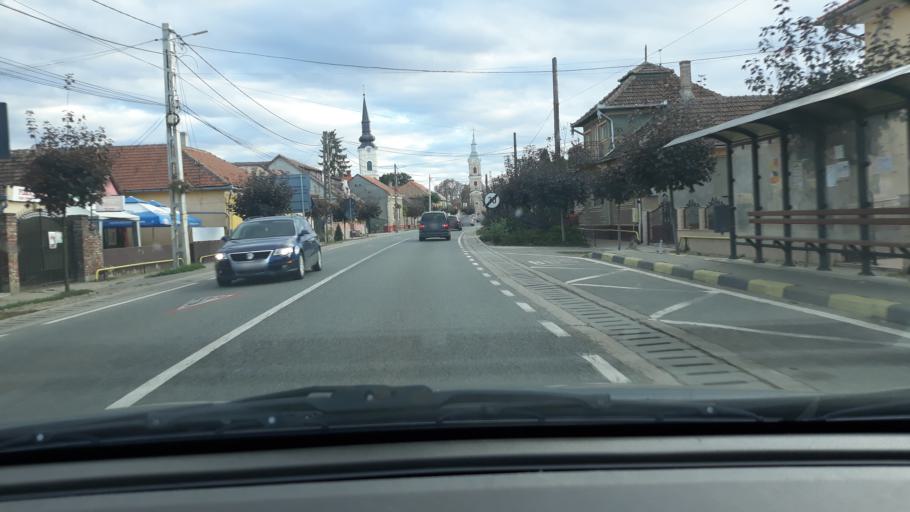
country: RO
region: Bihor
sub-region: Comuna Biharea
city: Biharea
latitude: 47.1555
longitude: 21.9215
